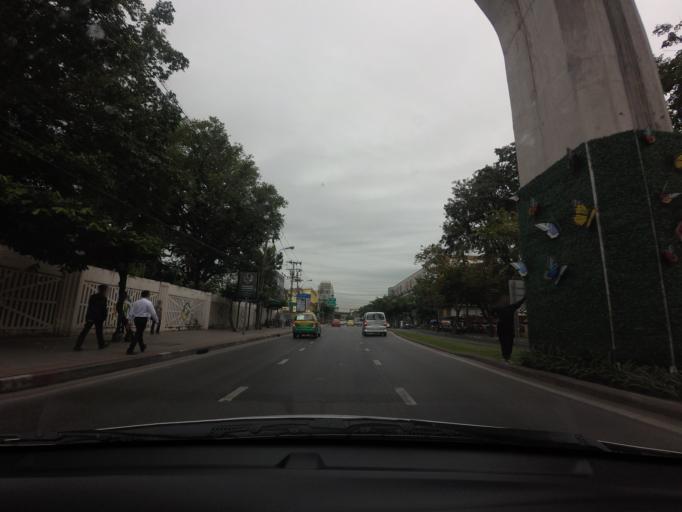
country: TH
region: Bangkok
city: Pathum Wan
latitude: 13.7460
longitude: 100.5242
